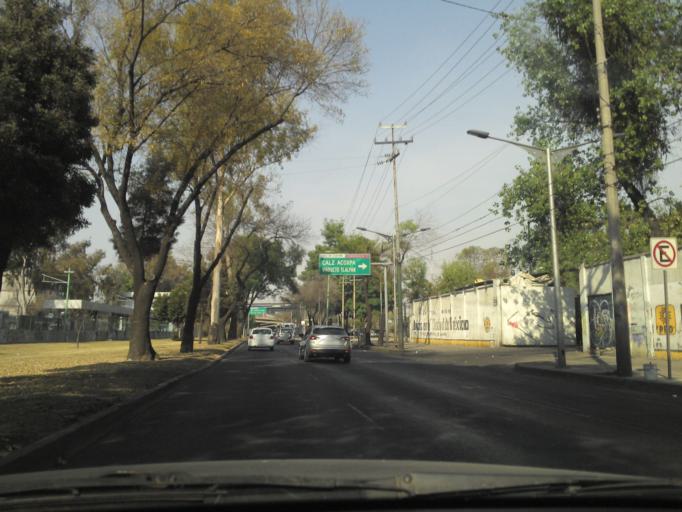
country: MX
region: Mexico City
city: Tlalpan
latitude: 19.3061
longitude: -99.1436
